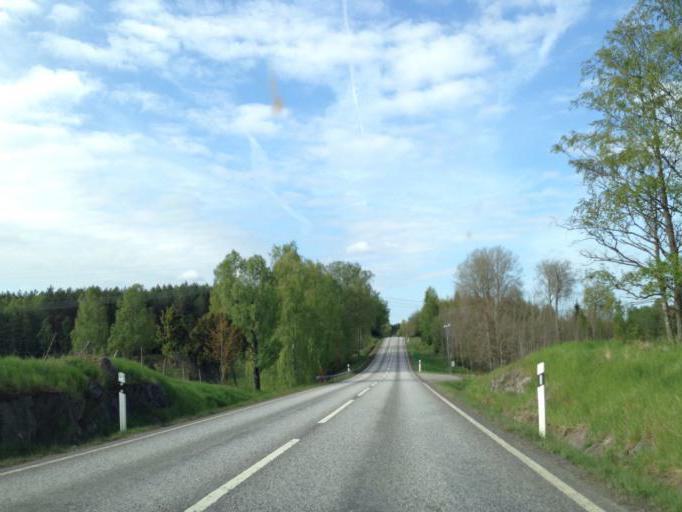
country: SE
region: Soedermanland
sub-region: Nykopings Kommun
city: Stigtomta
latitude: 58.9507
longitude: 16.8533
